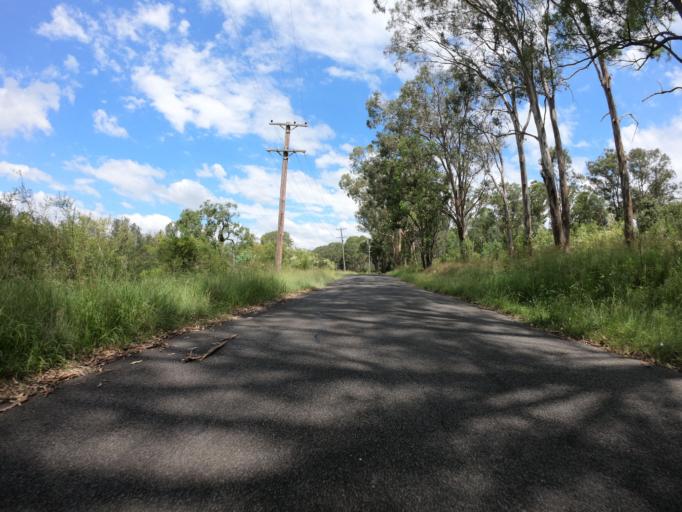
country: AU
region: New South Wales
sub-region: Penrith Municipality
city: Mulgoa
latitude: -33.8284
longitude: 150.6567
